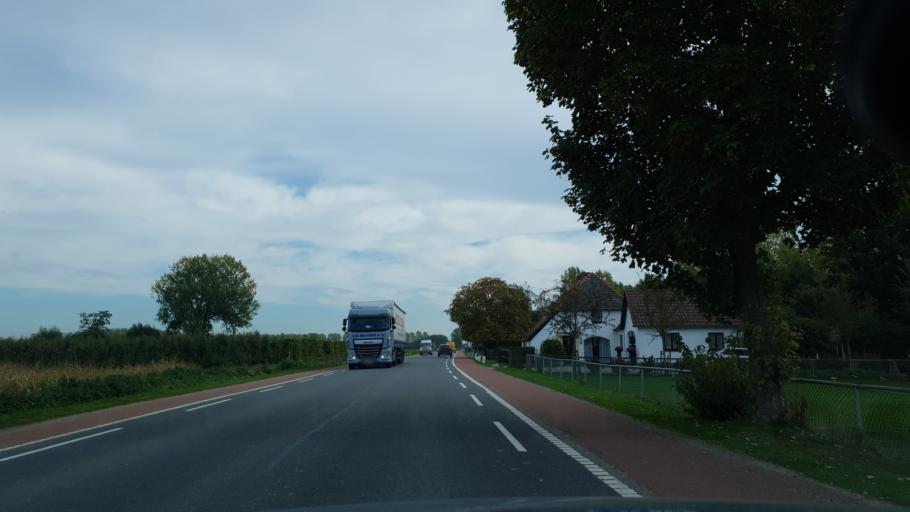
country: NL
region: Gelderland
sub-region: Gemeente Wijchen
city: Bergharen
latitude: 51.8813
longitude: 5.6697
